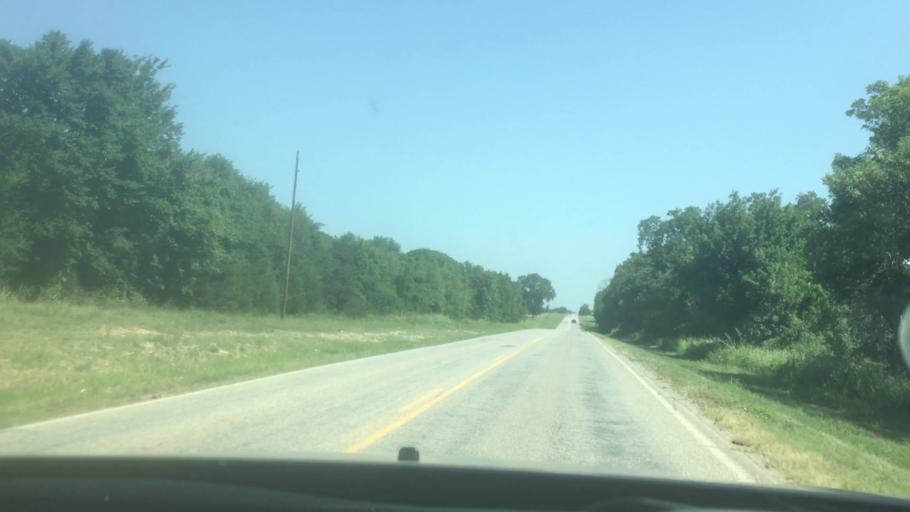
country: US
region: Oklahoma
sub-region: Johnston County
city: Tishomingo
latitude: 34.2954
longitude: -96.4248
